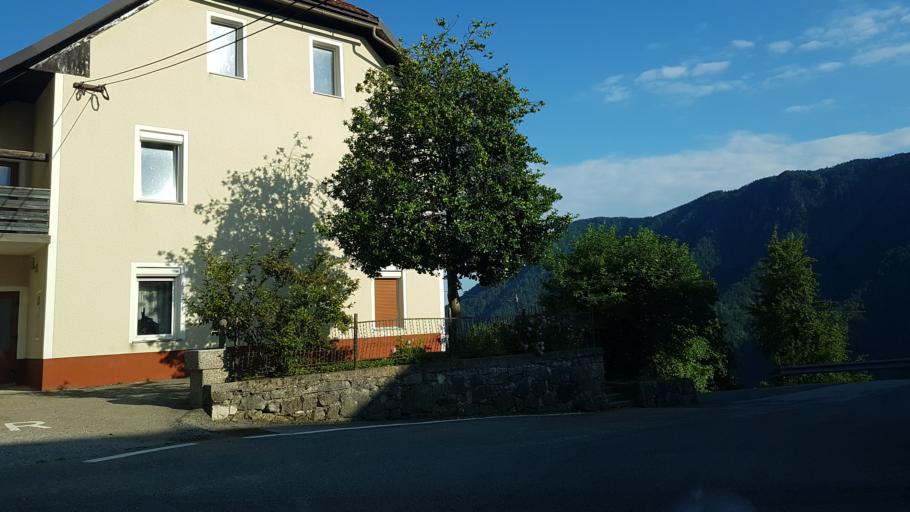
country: SI
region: Cerkno
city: Cerkno
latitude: 46.0795
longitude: 13.9918
